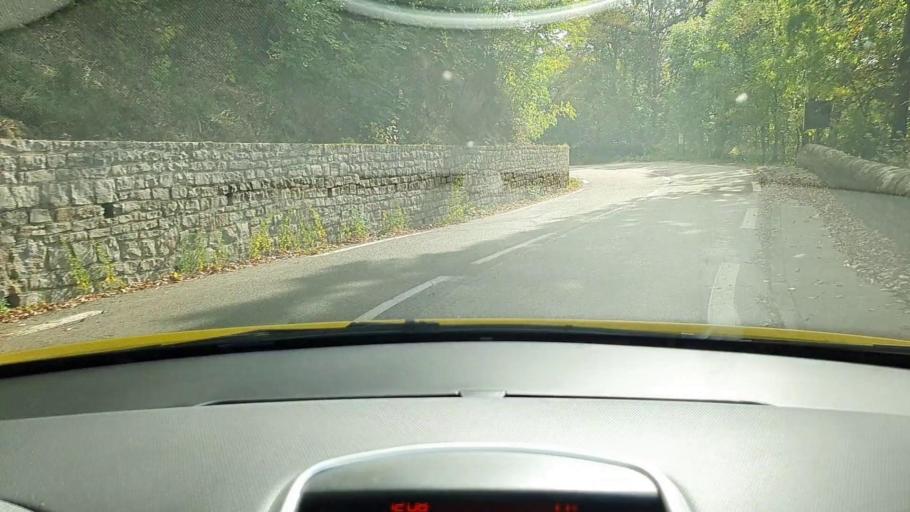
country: FR
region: Languedoc-Roussillon
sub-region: Departement de la Lozere
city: Meyrueis
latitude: 44.1240
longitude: 3.4764
